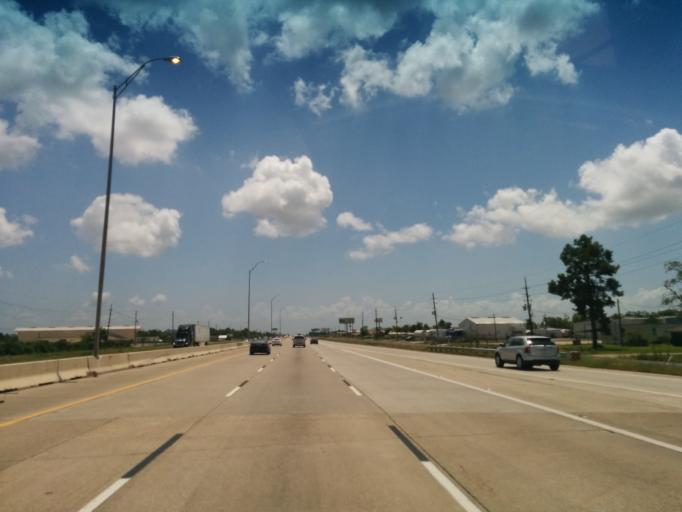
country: US
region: Texas
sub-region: Chambers County
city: Mont Belvieu
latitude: 29.8220
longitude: -94.8939
